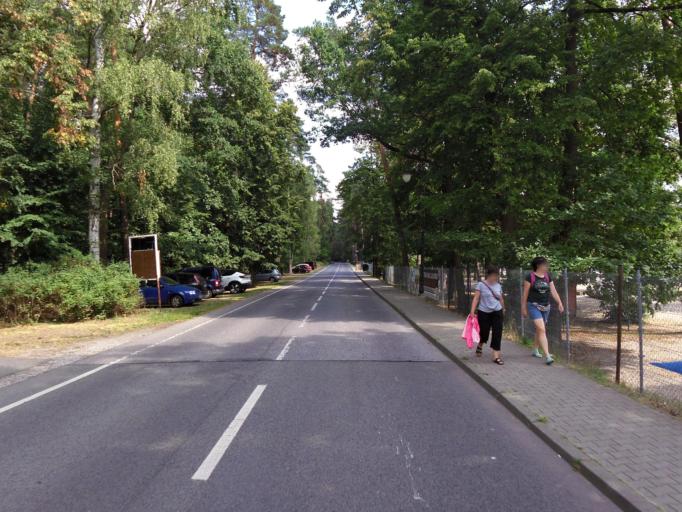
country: CZ
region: Liberecky
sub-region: Okres Ceska Lipa
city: Straz pod Ralskem
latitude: 50.7022
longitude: 14.8425
